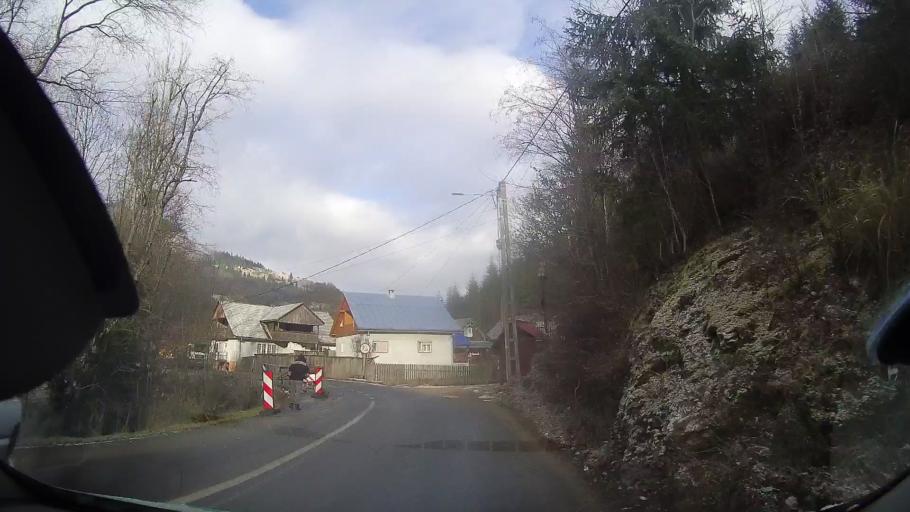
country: RO
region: Alba
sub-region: Comuna Albac
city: Albac
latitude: 46.4613
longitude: 22.9729
